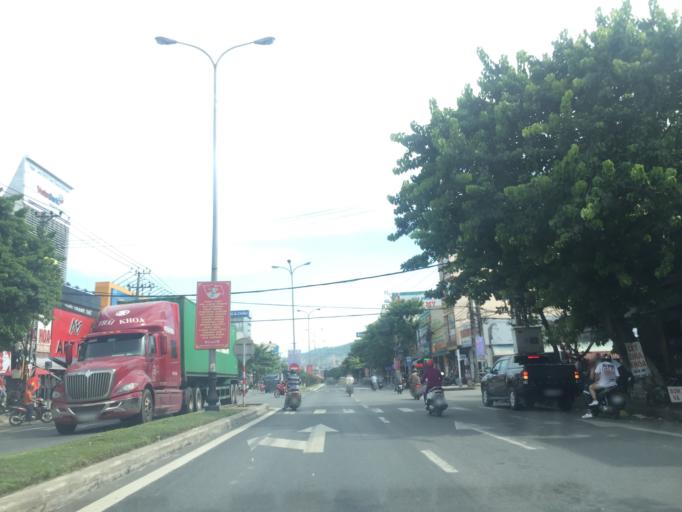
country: VN
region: Da Nang
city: Lien Chieu
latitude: 16.0722
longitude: 108.1503
